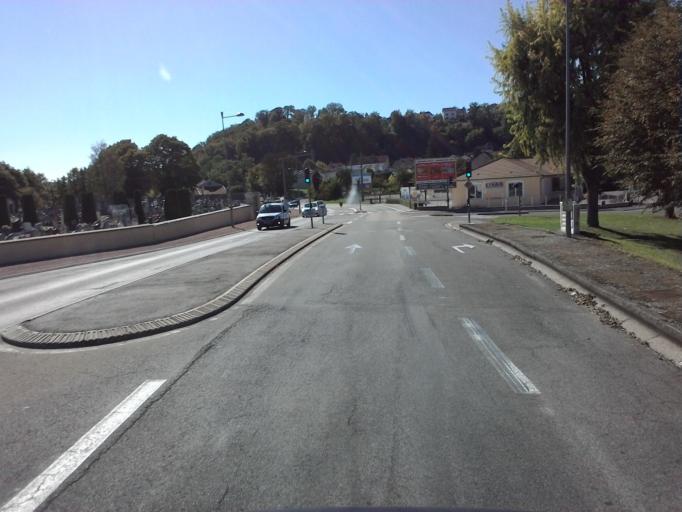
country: FR
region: Champagne-Ardenne
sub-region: Departement de la Haute-Marne
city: Chaumont
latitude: 48.1202
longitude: 5.1494
